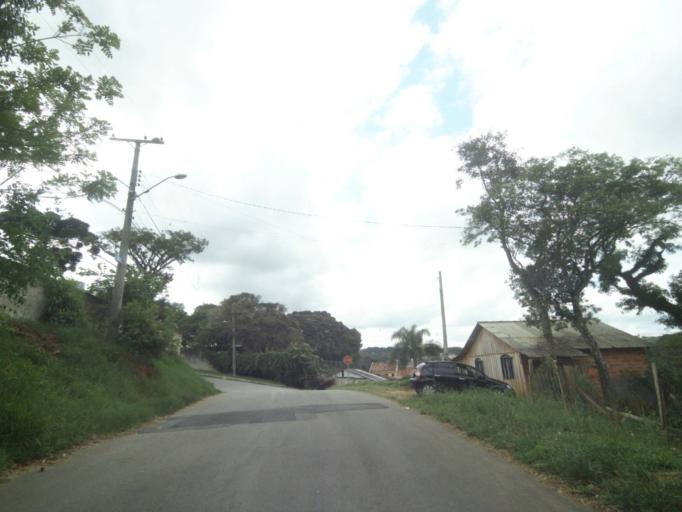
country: BR
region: Parana
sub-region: Curitiba
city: Curitiba
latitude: -25.3800
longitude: -49.2944
